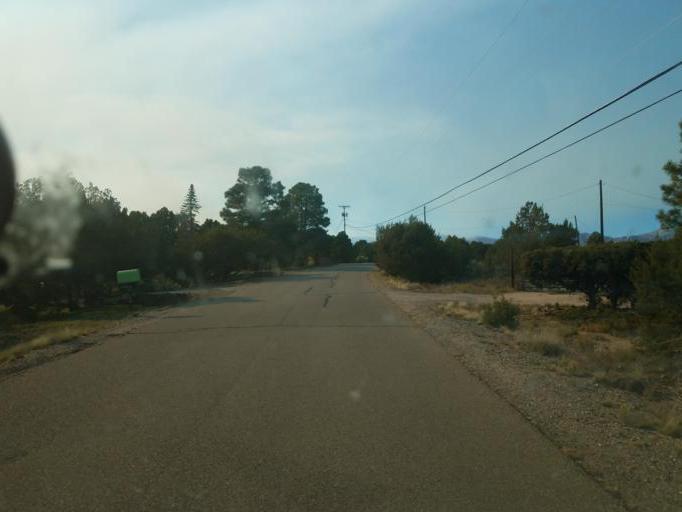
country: US
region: New Mexico
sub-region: Los Alamos County
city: White Rock
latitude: 35.8081
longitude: -106.2199
